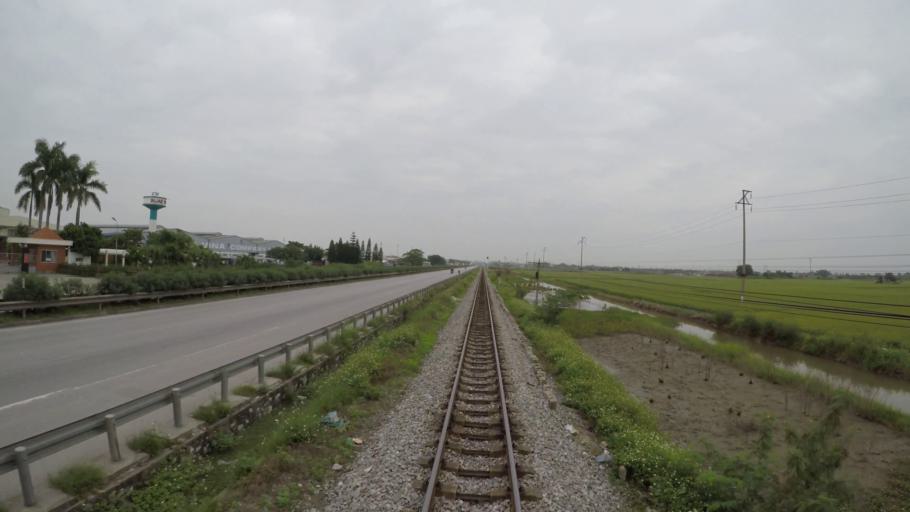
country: VN
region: Hai Duong
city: Phu Thai
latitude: 20.9645
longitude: 106.5158
